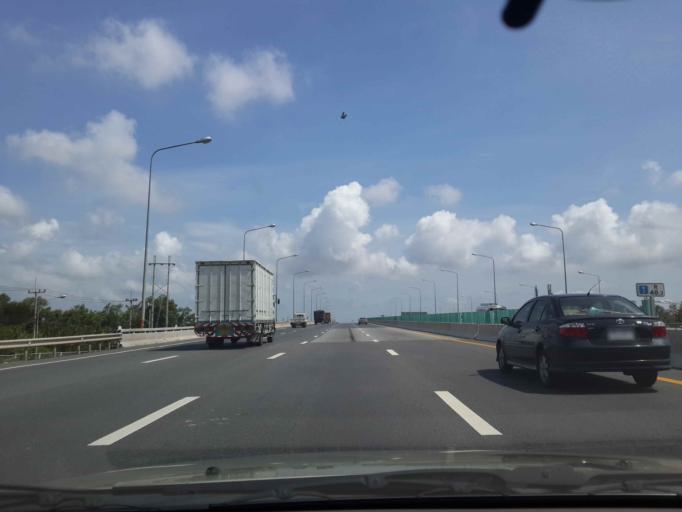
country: TH
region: Chachoengsao
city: Bang Pakong
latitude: 13.5462
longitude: 101.0030
